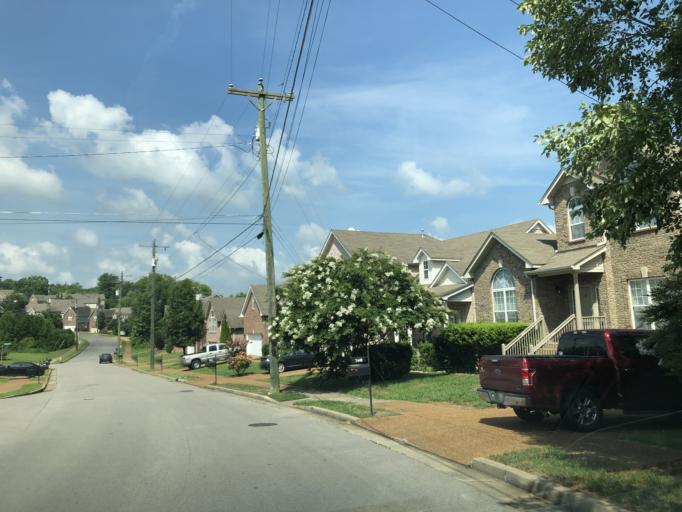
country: US
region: Tennessee
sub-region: Williamson County
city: Nolensville
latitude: 36.0111
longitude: -86.6852
